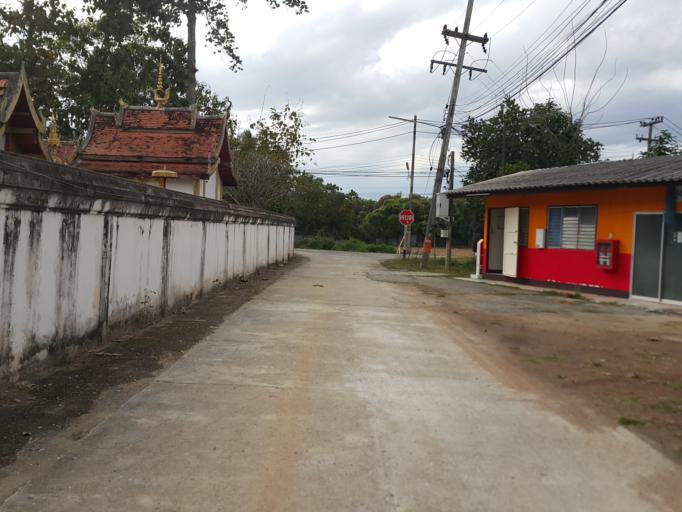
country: TH
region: Chiang Mai
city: San Sai
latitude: 18.8765
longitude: 99.0984
